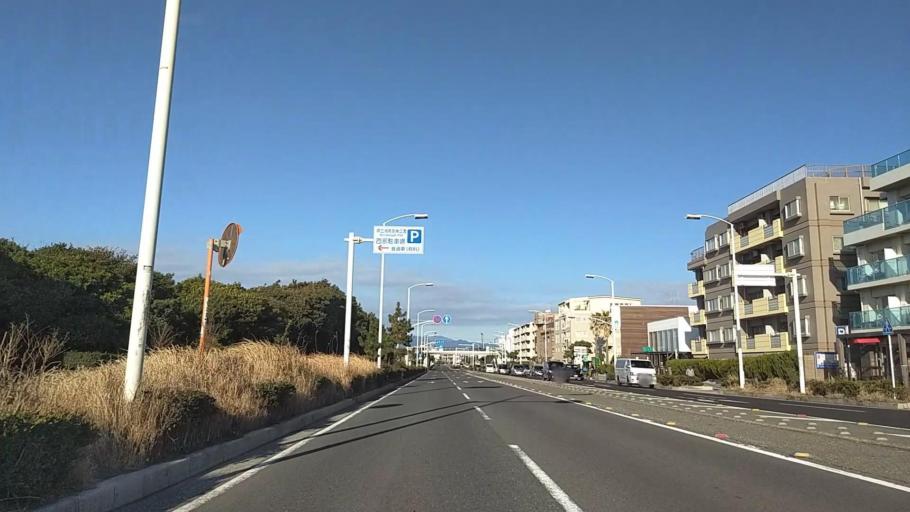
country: JP
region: Kanagawa
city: Fujisawa
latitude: 35.3141
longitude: 139.4755
